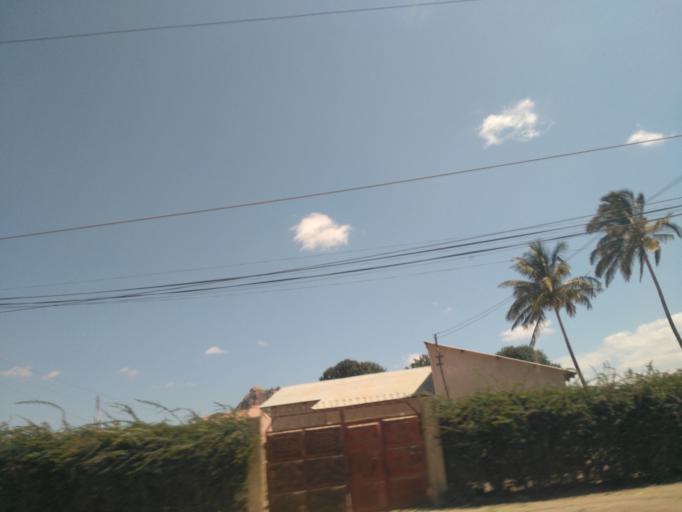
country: TZ
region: Dodoma
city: Dodoma
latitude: -6.1650
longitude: 35.7655
